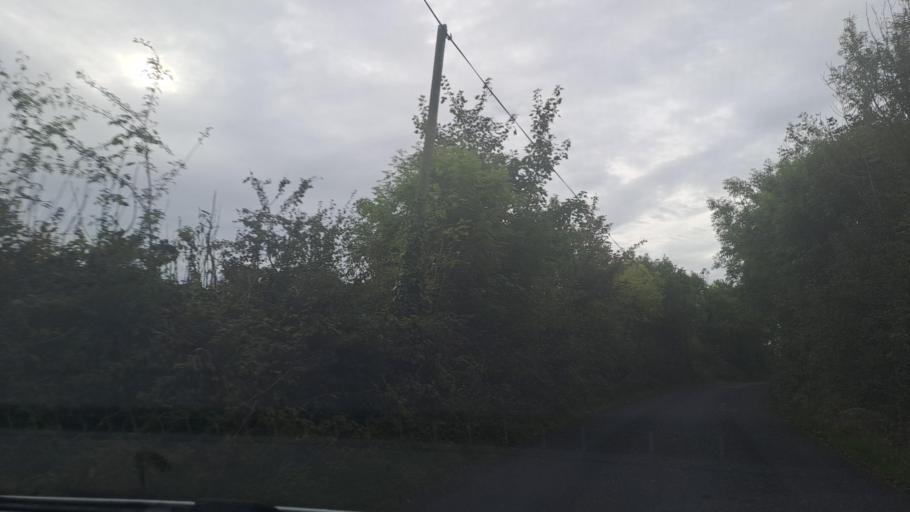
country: IE
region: Ulster
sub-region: County Monaghan
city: Carrickmacross
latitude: 53.9802
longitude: -6.7549
